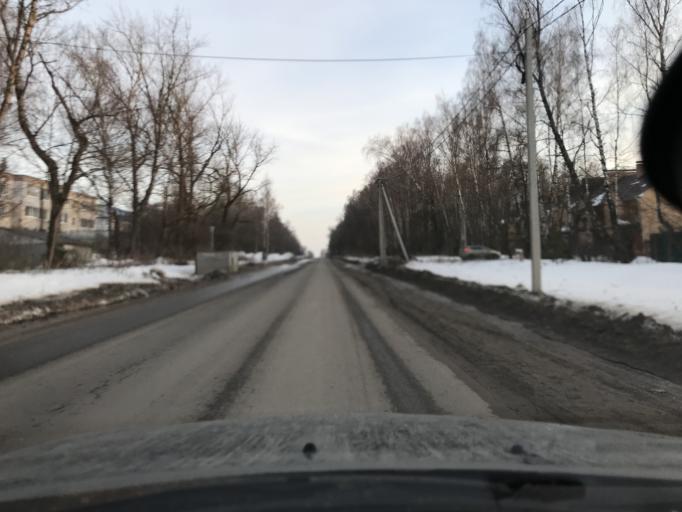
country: RU
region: Kaluga
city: Kaluga
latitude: 54.4848
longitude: 36.2449
